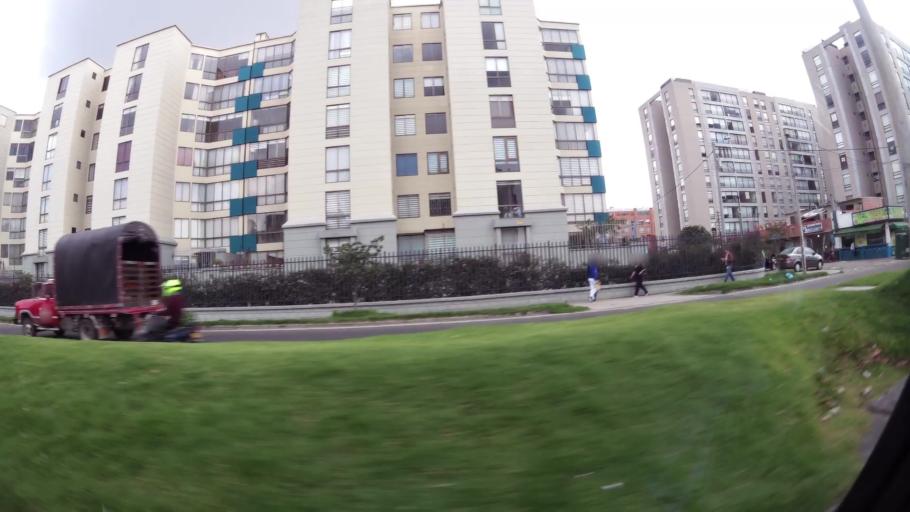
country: CO
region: Bogota D.C.
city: Barrio San Luis
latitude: 4.7284
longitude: -74.0391
